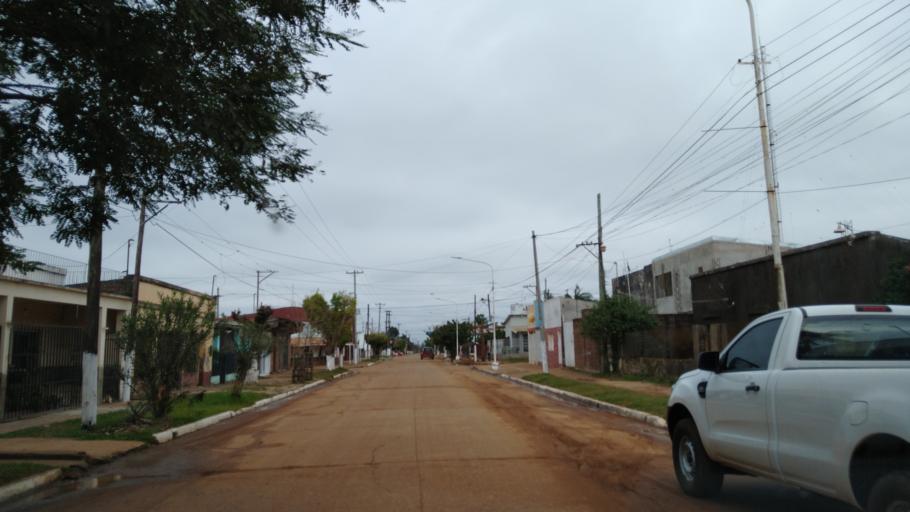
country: AR
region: Corrientes
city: Alvear
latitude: -29.0939
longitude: -56.5476
